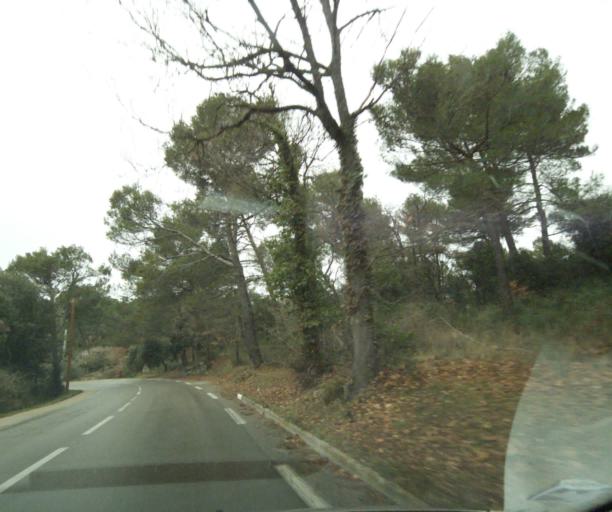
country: FR
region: Provence-Alpes-Cote d'Azur
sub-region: Departement des Bouches-du-Rhone
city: Rognes
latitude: 43.6617
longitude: 5.3697
